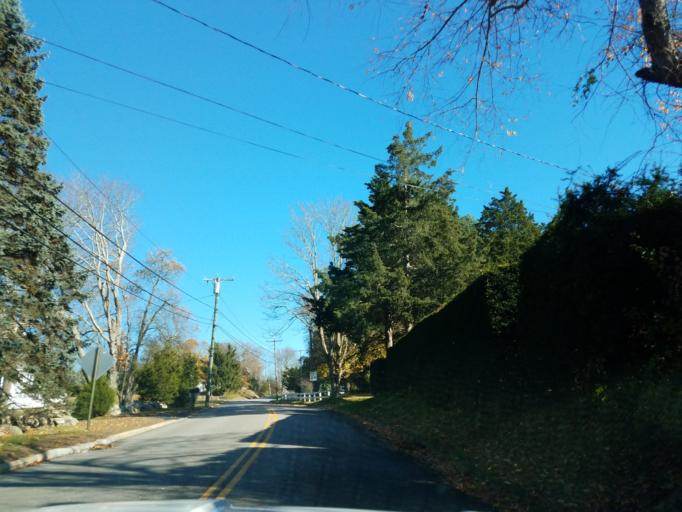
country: US
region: Connecticut
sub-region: New London County
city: Central Waterford
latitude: 41.3236
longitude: -72.1459
